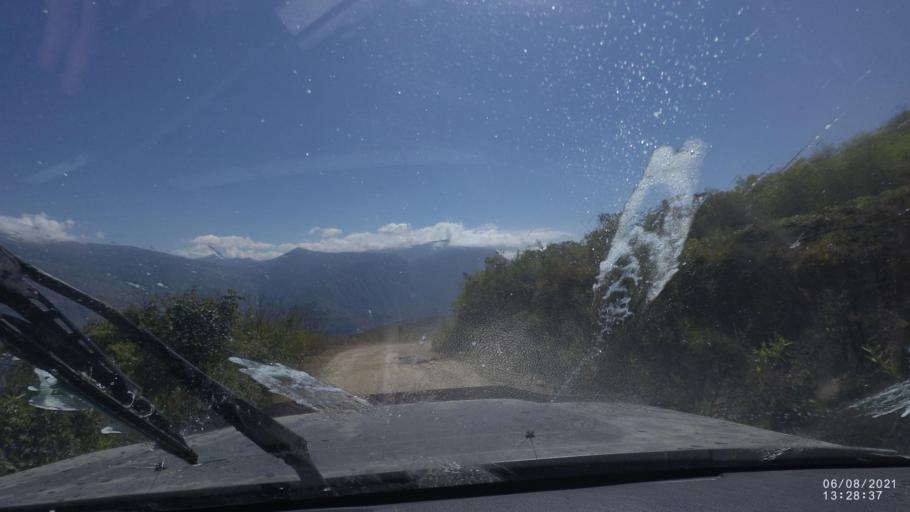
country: BO
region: La Paz
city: Quime
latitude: -16.6997
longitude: -66.7223
